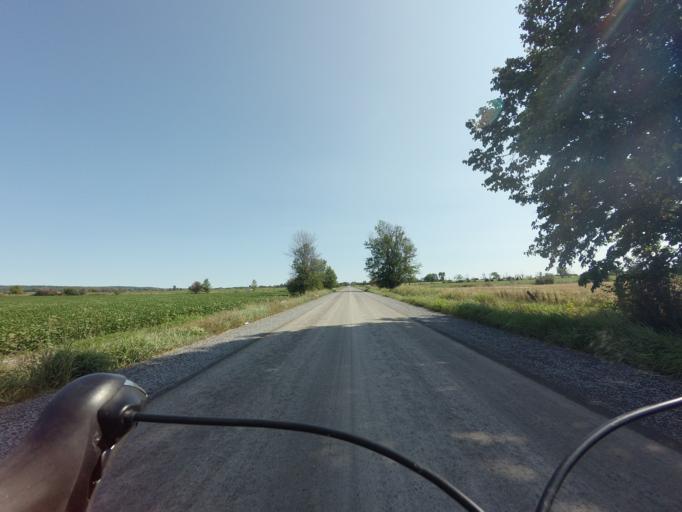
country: CA
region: Ontario
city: Arnprior
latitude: 45.3717
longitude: -76.1396
